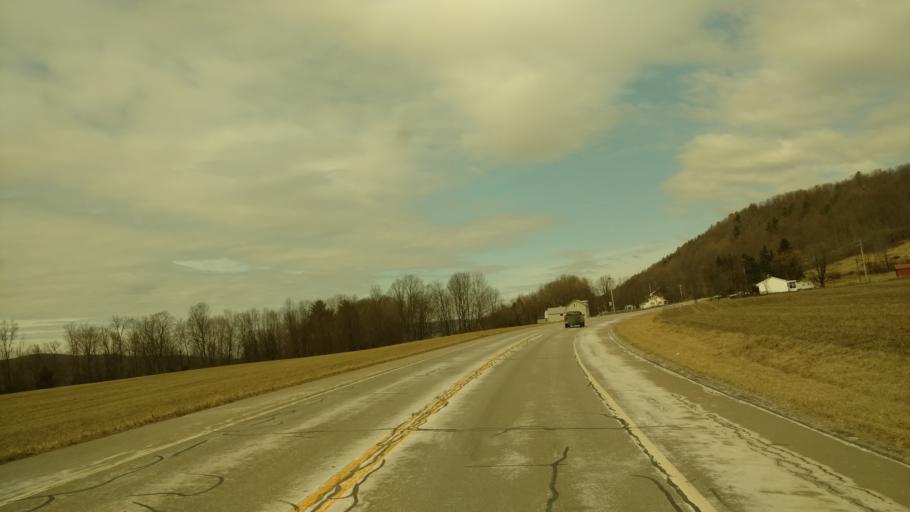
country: US
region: New York
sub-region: Allegany County
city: Wellsville
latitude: 42.0644
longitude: -77.9201
